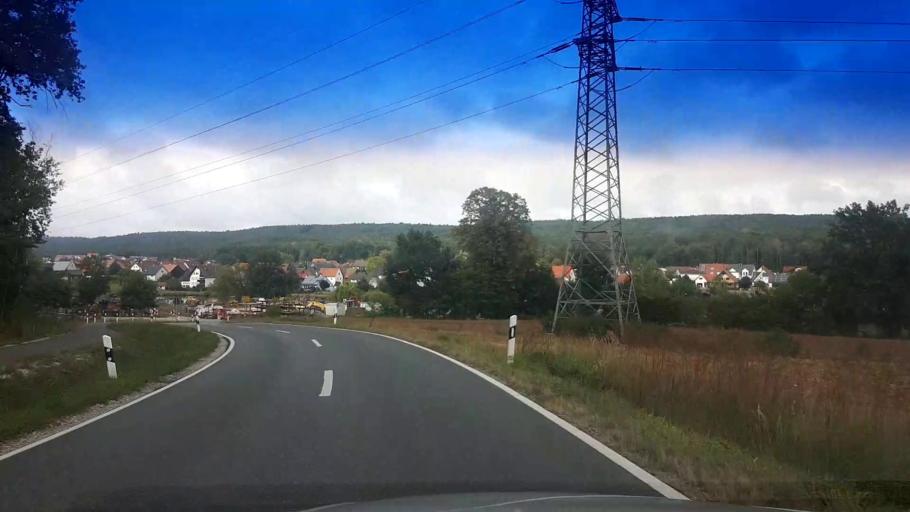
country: DE
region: Bavaria
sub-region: Upper Franconia
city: Heroldsbach
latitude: 49.7019
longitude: 11.0109
